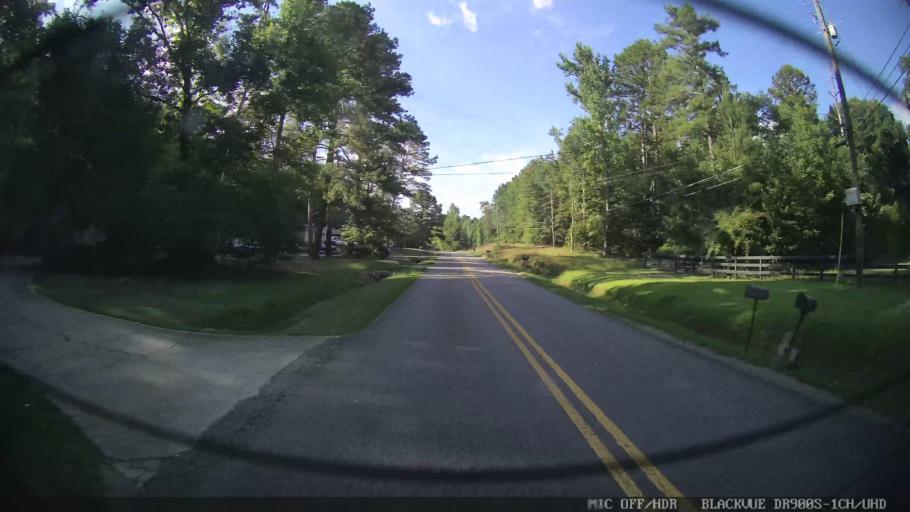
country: US
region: Georgia
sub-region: Floyd County
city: Rome
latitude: 34.2251
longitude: -85.1378
